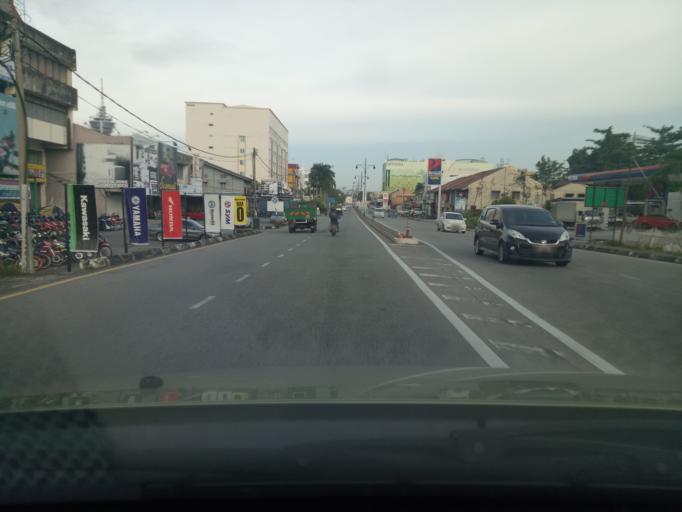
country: MY
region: Kedah
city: Alor Setar
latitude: 6.1240
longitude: 100.3603
